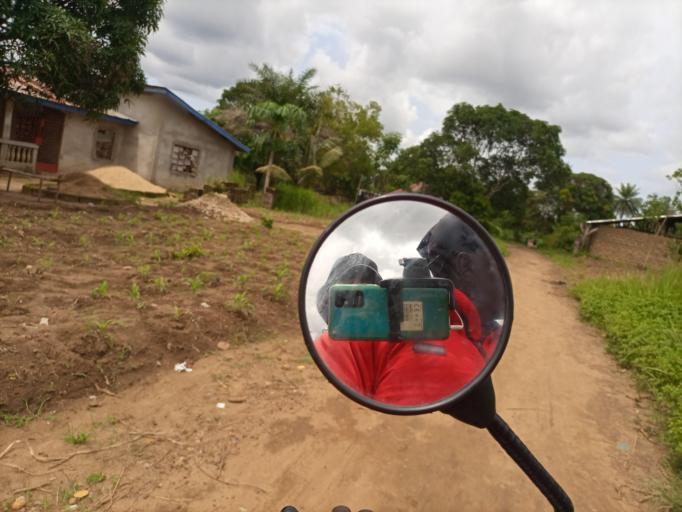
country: SL
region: Southern Province
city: Bo
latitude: 7.9682
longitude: -11.7149
